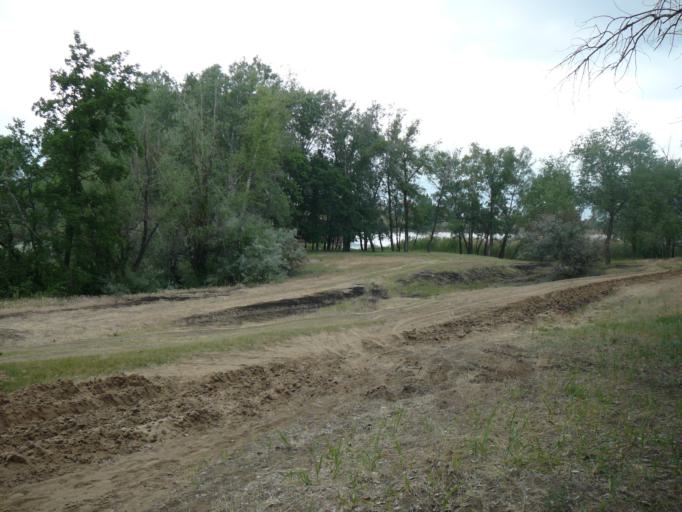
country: RU
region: Saratov
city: Engel's
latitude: 51.4920
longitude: 46.0609
